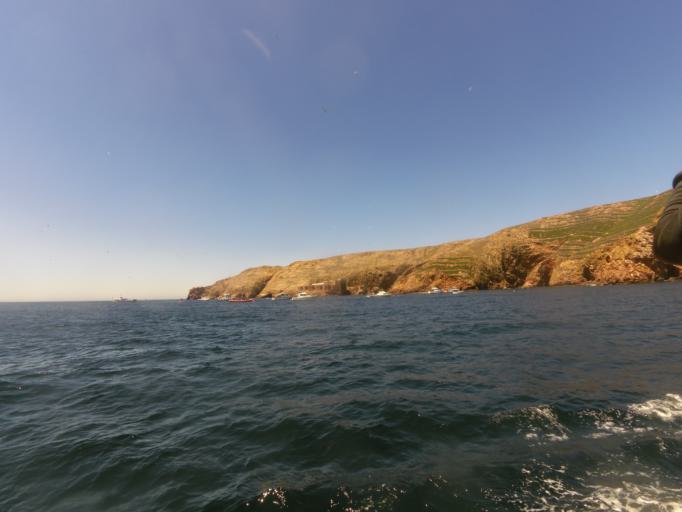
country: PT
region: Leiria
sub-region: Peniche
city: Peniche
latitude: 39.4125
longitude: -9.5047
